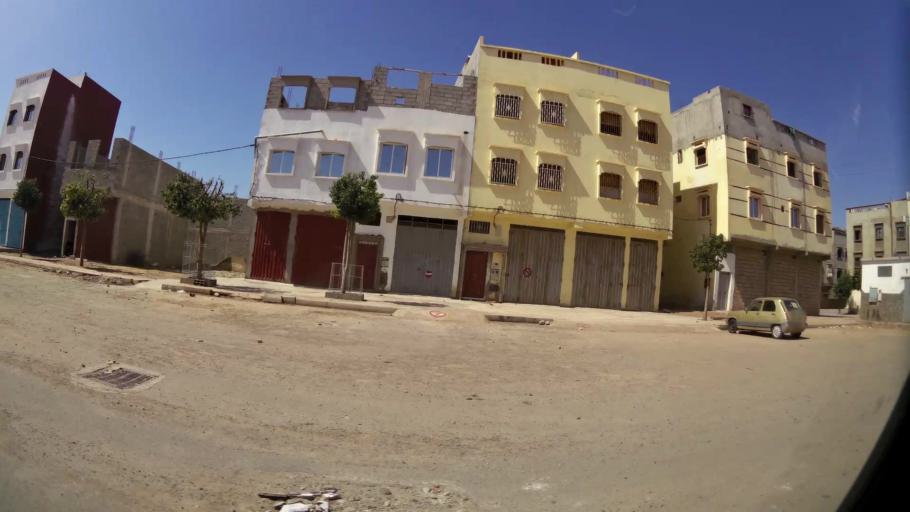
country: MA
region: Souss-Massa-Draa
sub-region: Inezgane-Ait Mellou
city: Inezgane
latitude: 30.3479
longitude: -9.5596
